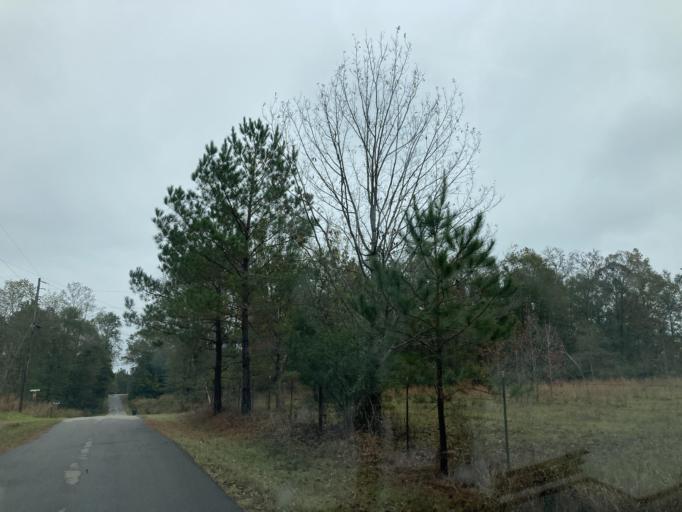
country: US
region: Mississippi
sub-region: Lamar County
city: Purvis
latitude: 31.2315
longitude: -89.5063
